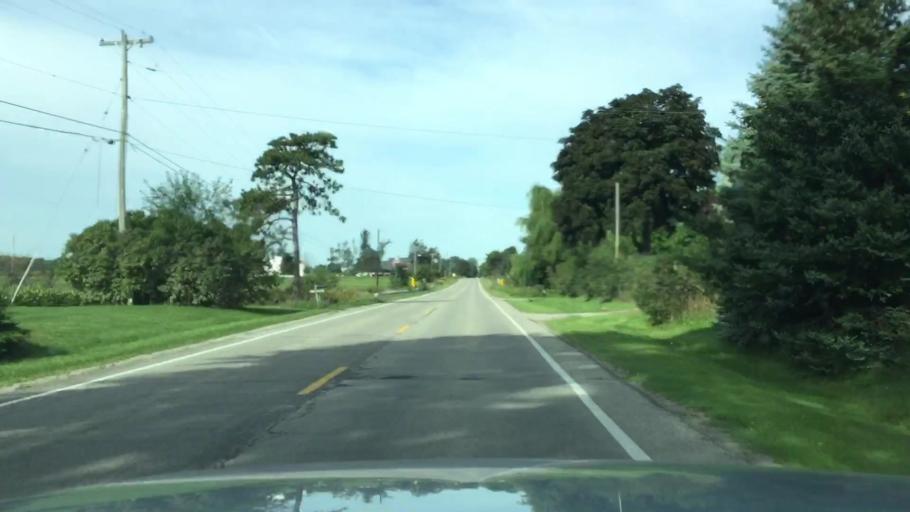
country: US
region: Michigan
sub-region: Genesee County
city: Montrose
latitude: 43.1178
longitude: -83.9071
